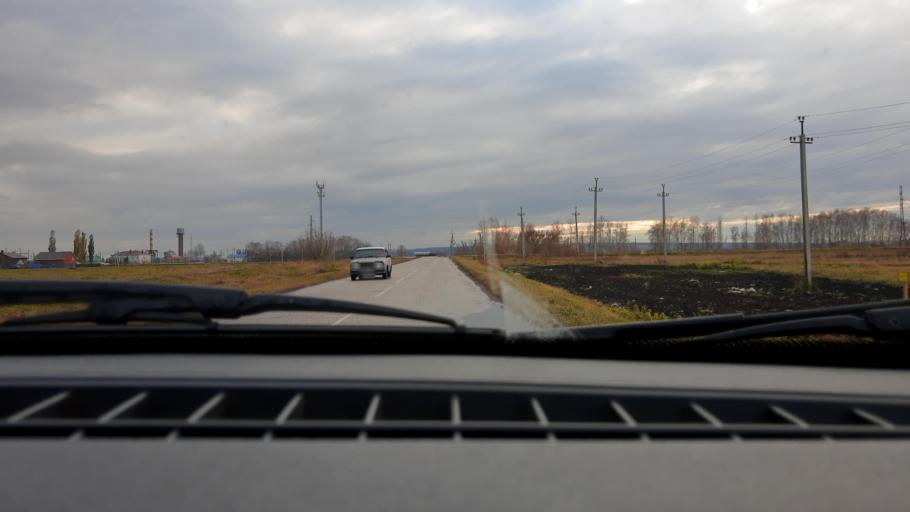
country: RU
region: Bashkortostan
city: Ufa
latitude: 54.8473
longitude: 56.0059
